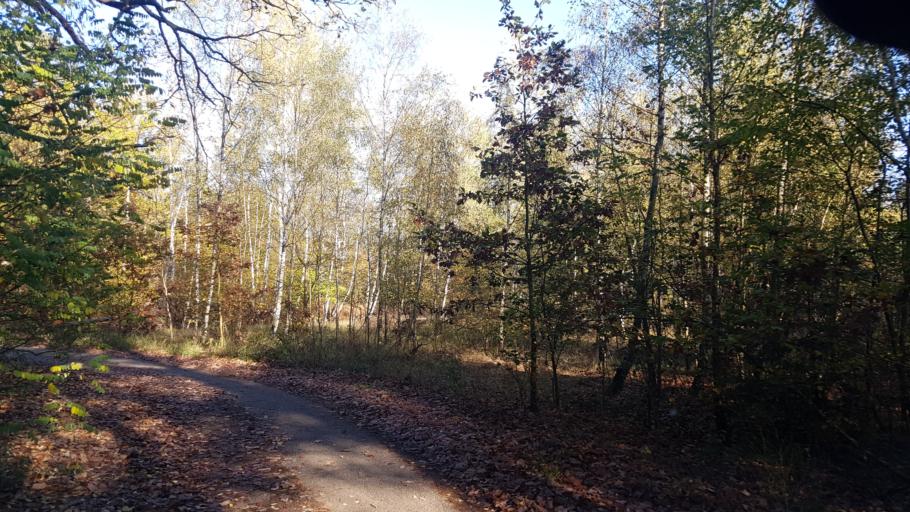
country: DE
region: Brandenburg
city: Hohenleipisch
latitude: 51.5440
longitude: 13.5353
